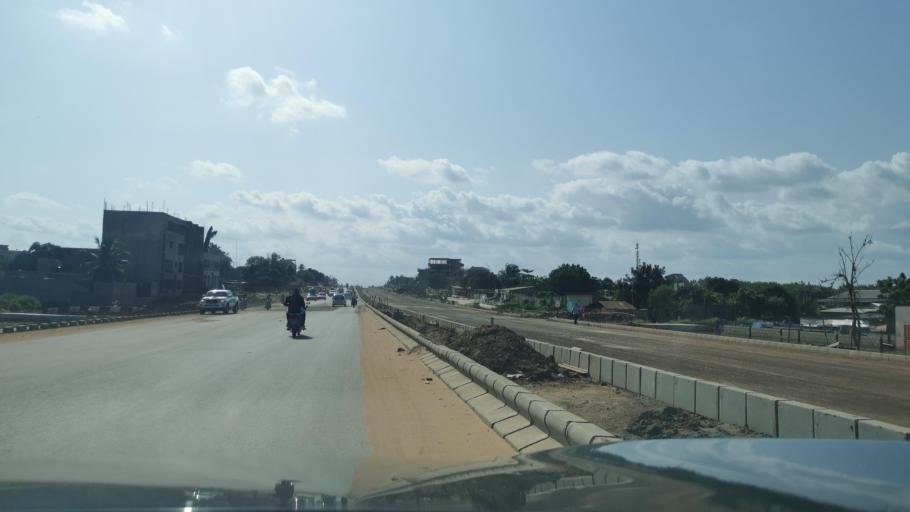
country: TG
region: Maritime
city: Lome
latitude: 6.2141
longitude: 1.1327
